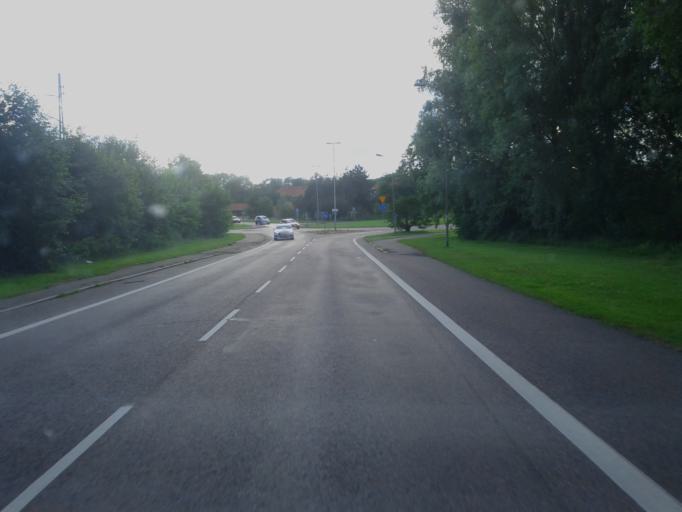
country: SE
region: Dalarna
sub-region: Borlange Kommun
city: Borlaenge
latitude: 60.4985
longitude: 15.4597
